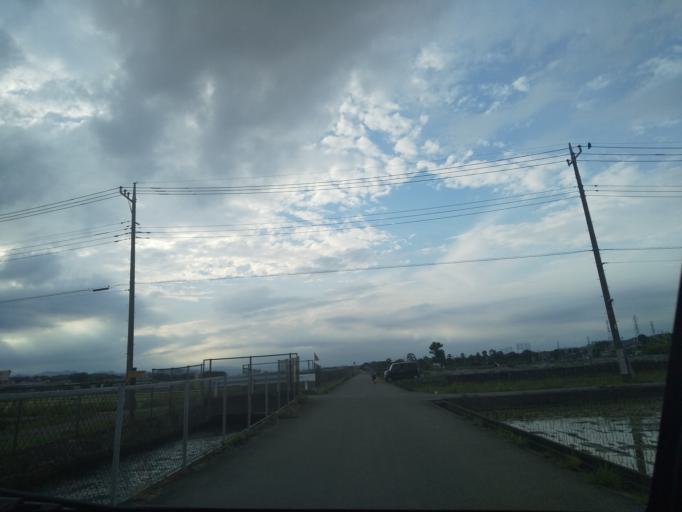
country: JP
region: Kanagawa
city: Zama
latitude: 35.5012
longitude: 139.3820
